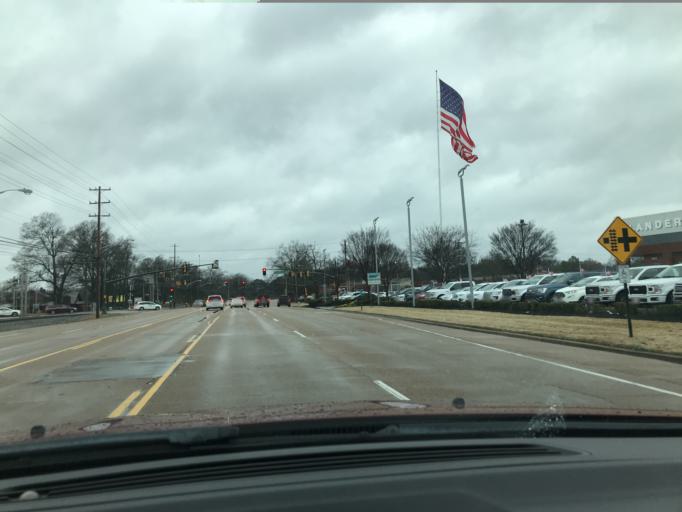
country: US
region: Tennessee
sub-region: Shelby County
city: Collierville
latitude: 35.0512
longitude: -89.7311
